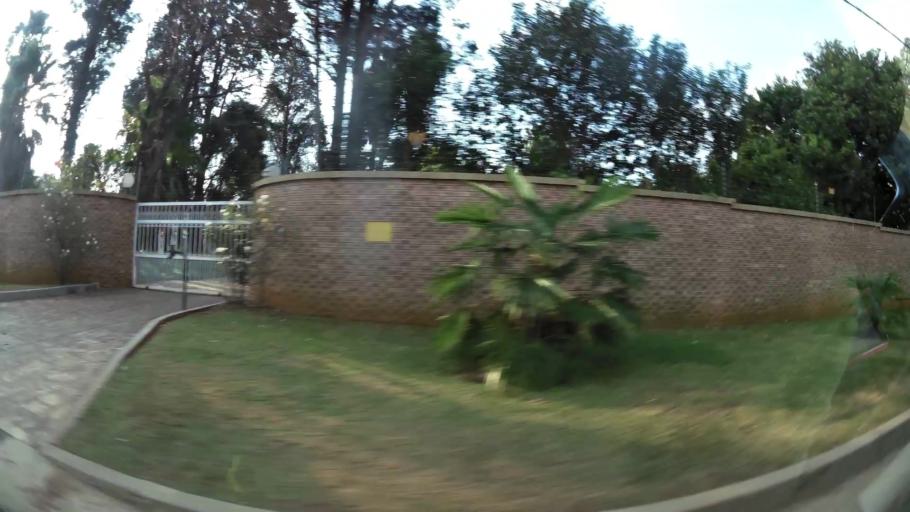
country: ZA
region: Gauteng
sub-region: Ekurhuleni Metropolitan Municipality
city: Benoni
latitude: -26.1201
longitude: 28.3036
